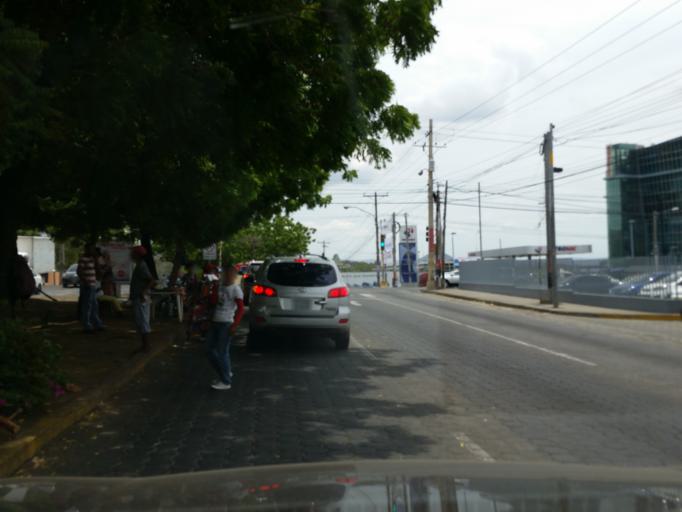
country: NI
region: Managua
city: Managua
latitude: 12.1126
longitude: -86.2648
